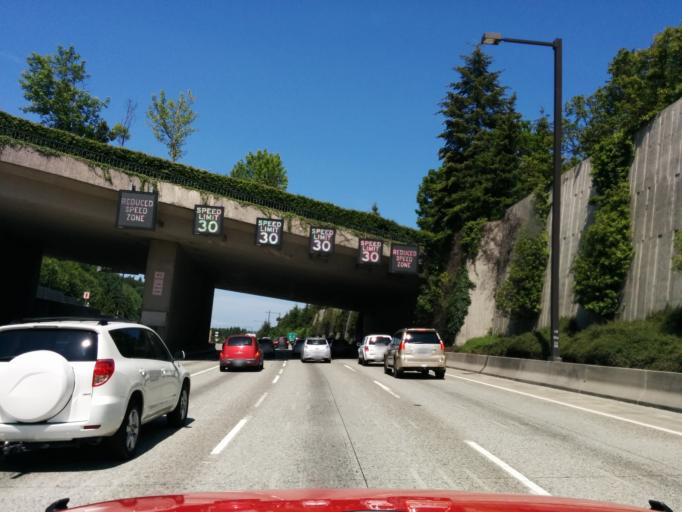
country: US
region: Washington
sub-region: King County
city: Mercer Island
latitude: 47.5819
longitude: -122.2186
